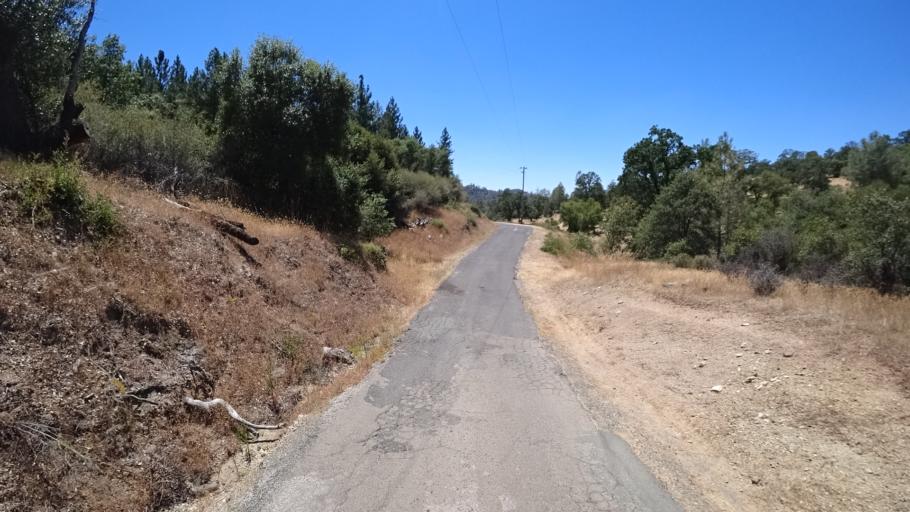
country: US
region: California
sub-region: Calaveras County
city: Mountain Ranch
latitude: 38.2677
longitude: -120.4668
